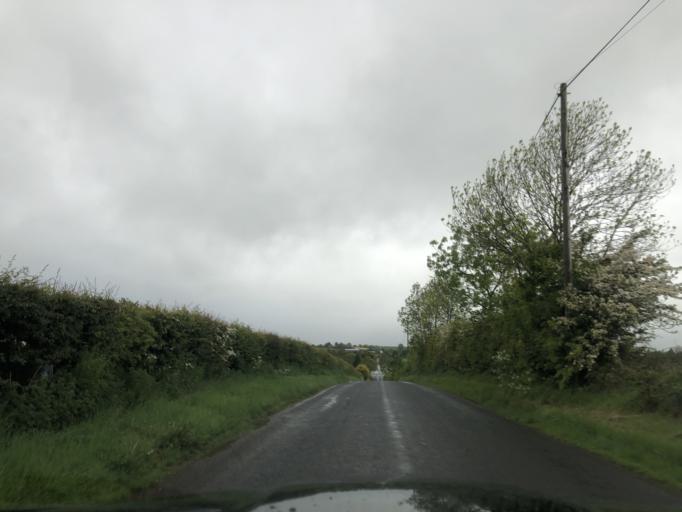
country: GB
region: Northern Ireland
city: Dunloy
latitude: 55.1210
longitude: -6.3591
